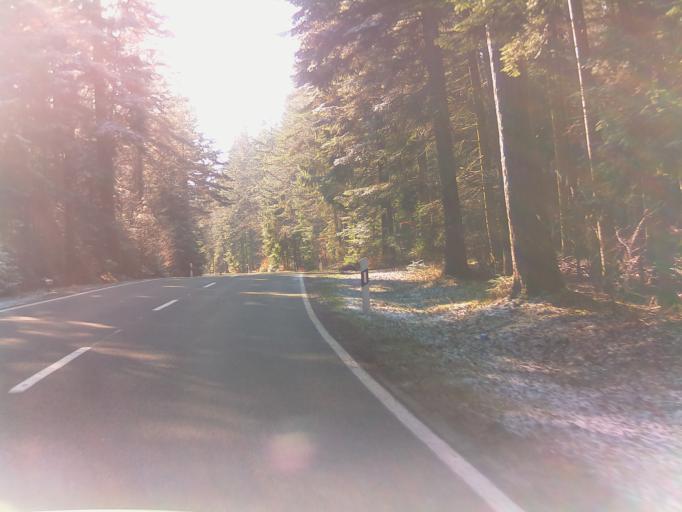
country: DE
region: Baden-Wuerttemberg
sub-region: Karlsruhe Region
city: Neuweiler
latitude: 48.6919
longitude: 8.5998
